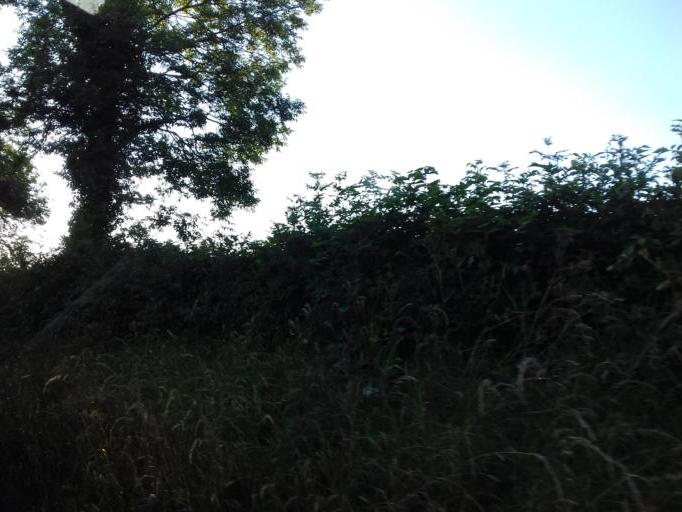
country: IE
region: Leinster
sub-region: An Mhi
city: Ashbourne
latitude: 53.5734
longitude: -6.3512
